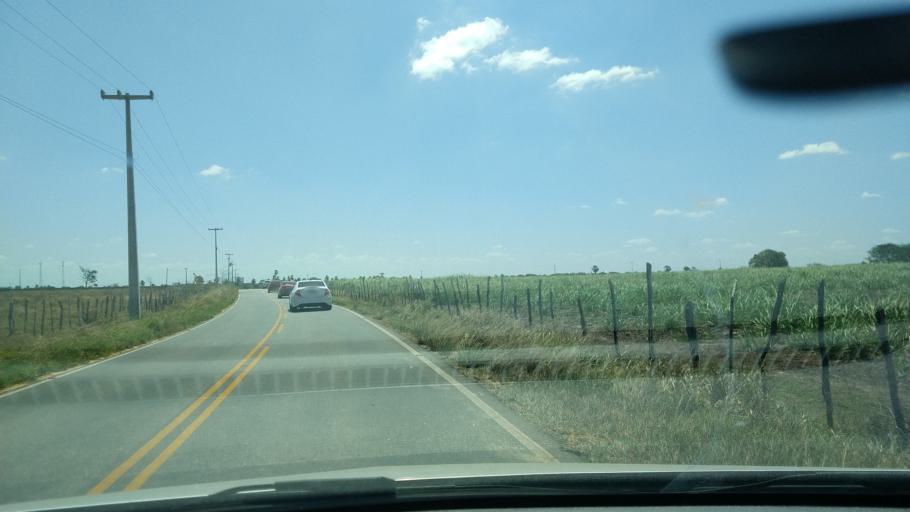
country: BR
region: Rio Grande do Norte
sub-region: Goianinha
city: Goianinha
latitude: -6.2595
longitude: -35.1977
